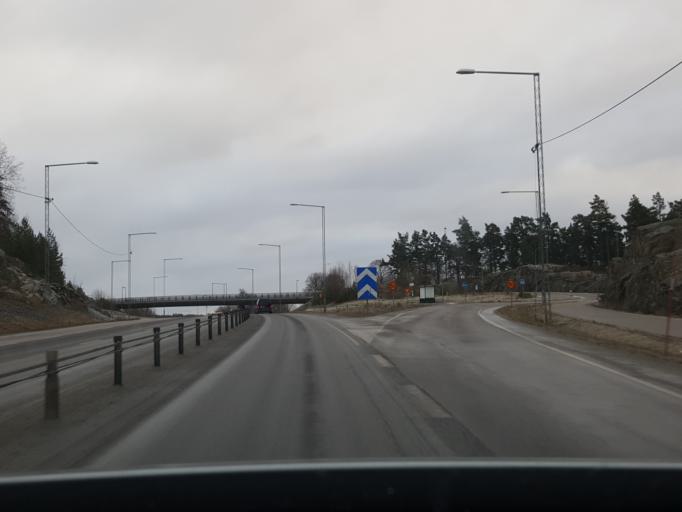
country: SE
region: Stockholm
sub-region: Botkyrka Kommun
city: Tumba
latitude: 59.2113
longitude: 17.8320
